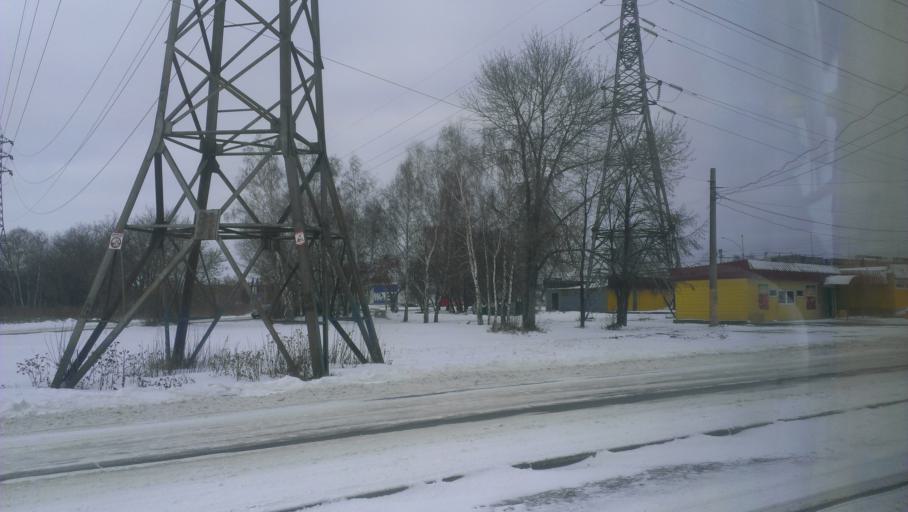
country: RU
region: Altai Krai
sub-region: Gorod Barnaulskiy
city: Barnaul
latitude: 53.3865
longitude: 83.7130
